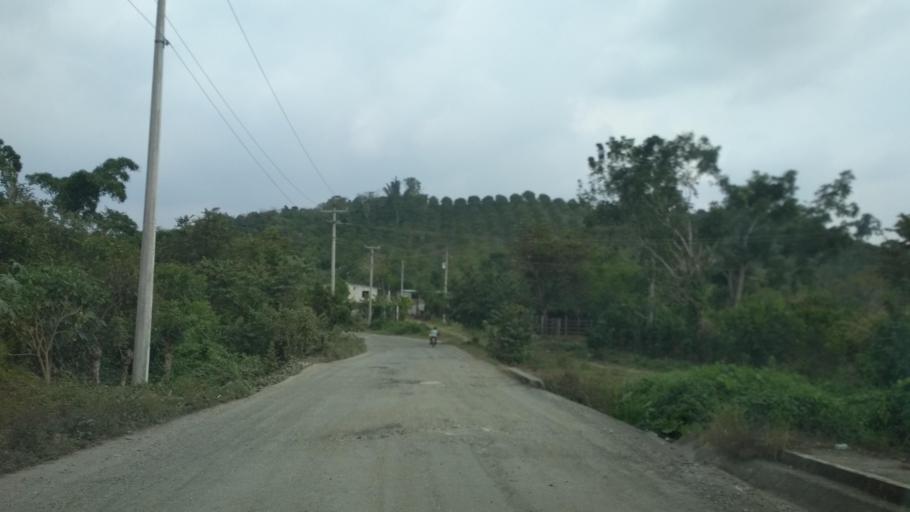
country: MM
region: Kayah
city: Loikaw
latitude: 20.2399
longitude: 97.2752
